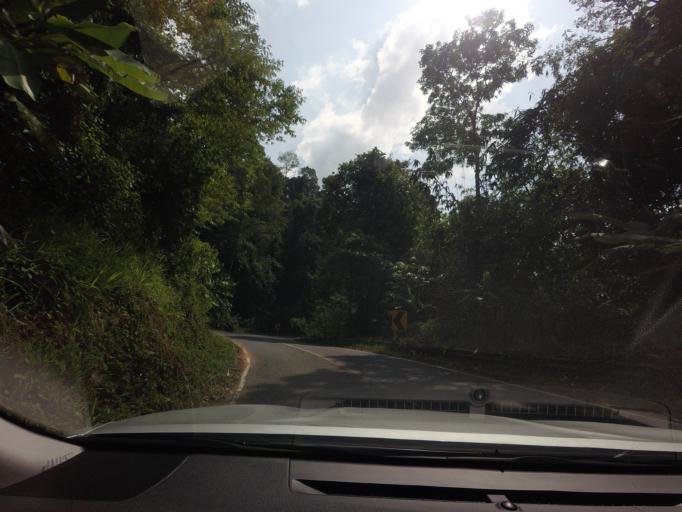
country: TH
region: Phangnga
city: Thap Put
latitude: 8.5373
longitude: 98.5623
